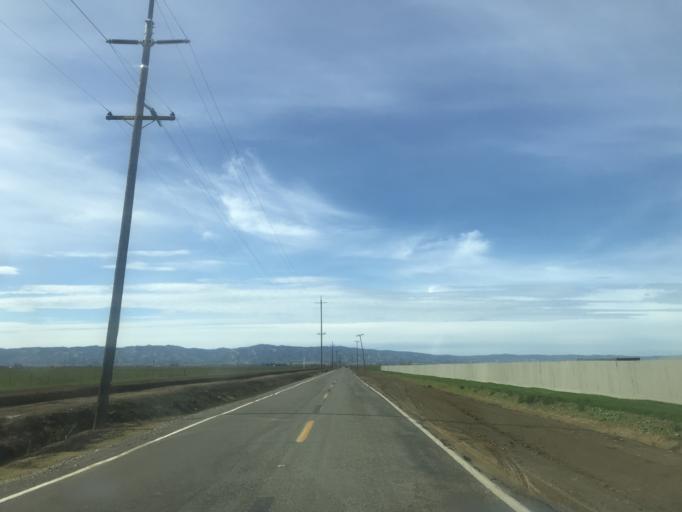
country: US
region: California
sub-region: Yolo County
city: Cottonwood
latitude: 38.6637
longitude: -121.9070
